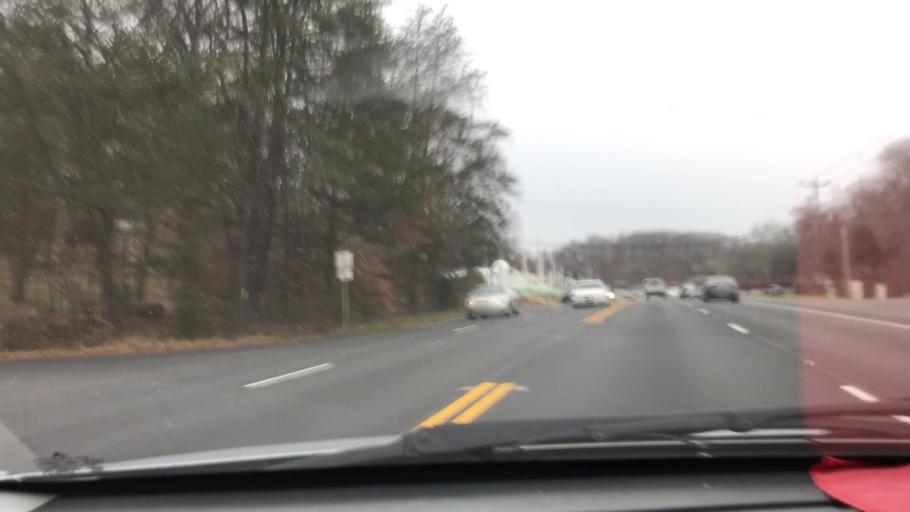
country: US
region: Virginia
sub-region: Prince William County
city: Triangle
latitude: 38.5109
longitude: -77.3697
